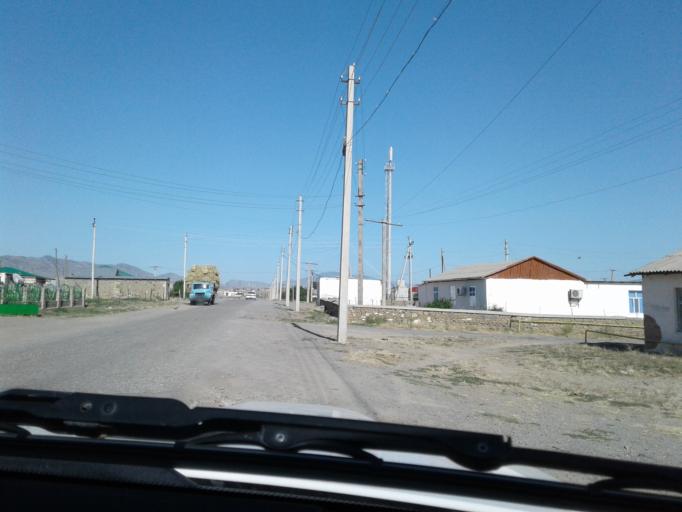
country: TM
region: Balkan
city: Magtymguly
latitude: 38.6834
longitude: 56.4545
